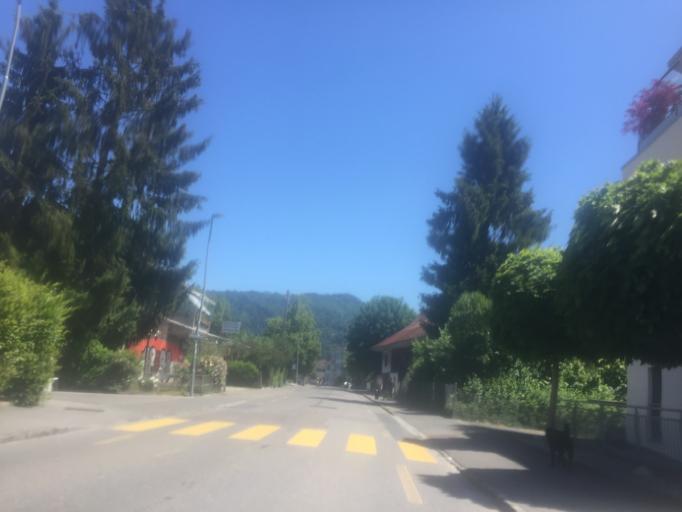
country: CH
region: Bern
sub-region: Thun District
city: Thun
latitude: 46.7493
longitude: 7.6154
